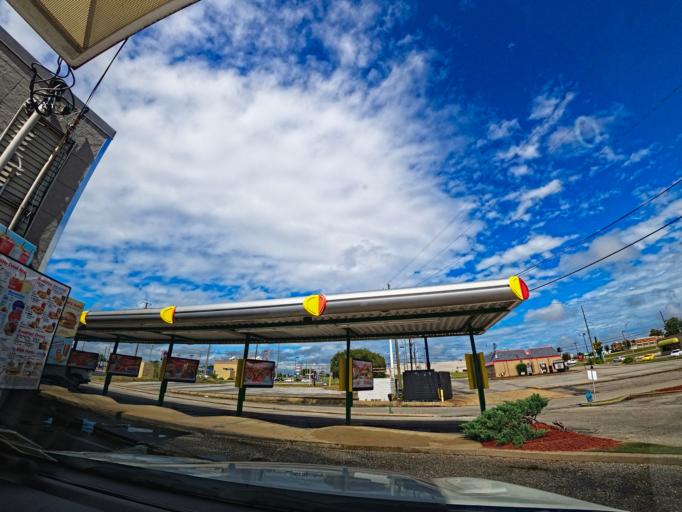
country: US
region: Alabama
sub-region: Tuscaloosa County
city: Tuscaloosa
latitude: 33.1669
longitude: -87.5239
